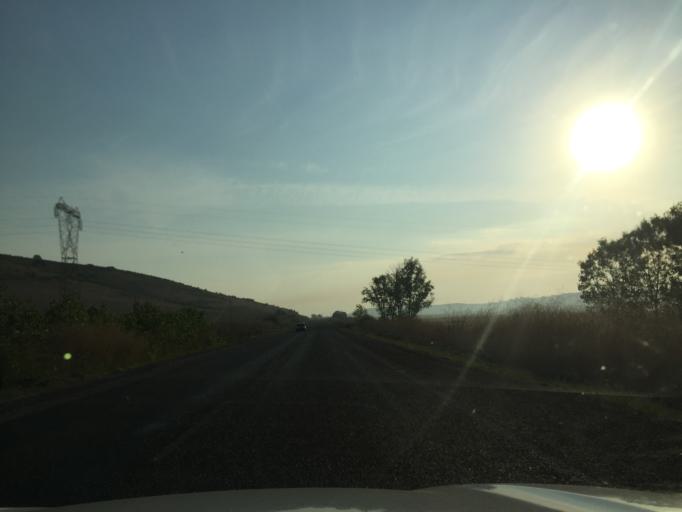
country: TR
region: Balikesir
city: Aksakal
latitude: 40.0865
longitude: 28.0994
